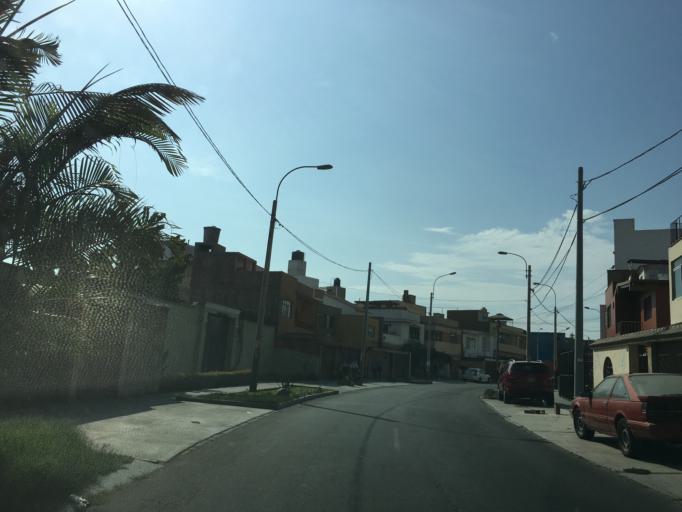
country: PE
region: Lima
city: Lima
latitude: -12.0693
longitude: -77.0673
